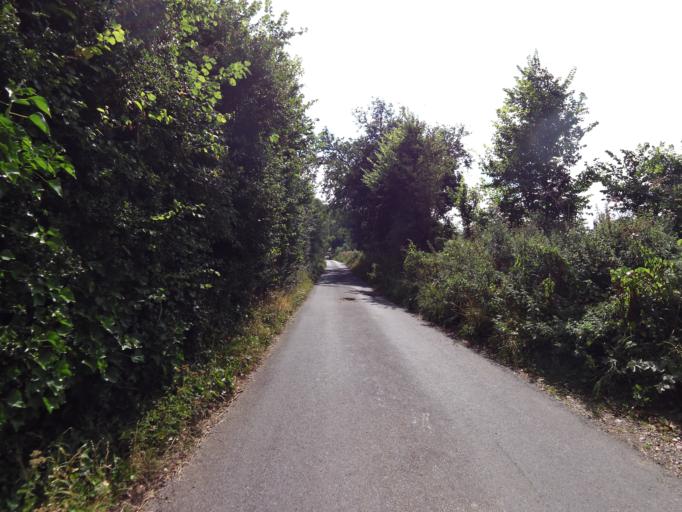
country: GB
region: England
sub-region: Hertfordshire
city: Shenley AV
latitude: 51.6943
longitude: -0.2477
